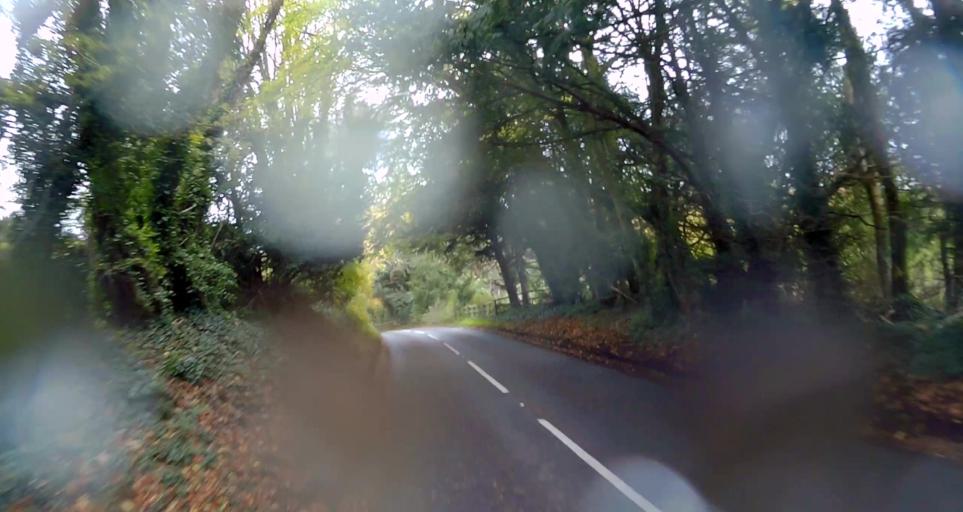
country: GB
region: England
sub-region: Hampshire
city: Kings Worthy
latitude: 51.1271
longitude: -1.1879
